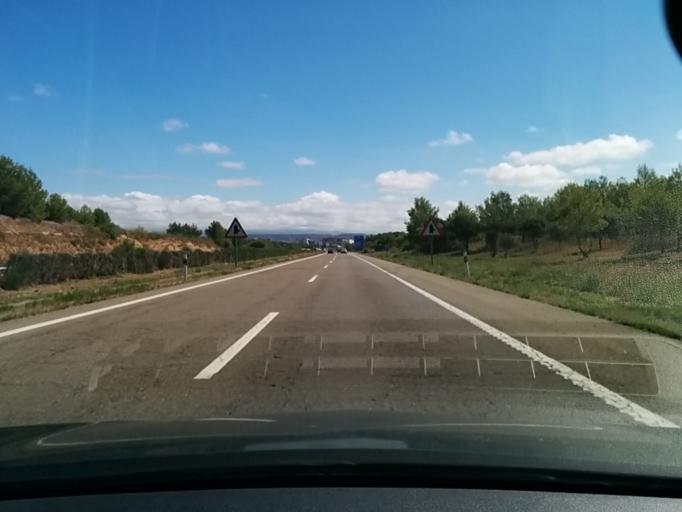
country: ES
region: Aragon
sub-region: Provincia de Huesca
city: Huesca
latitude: 42.1156
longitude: -0.4429
